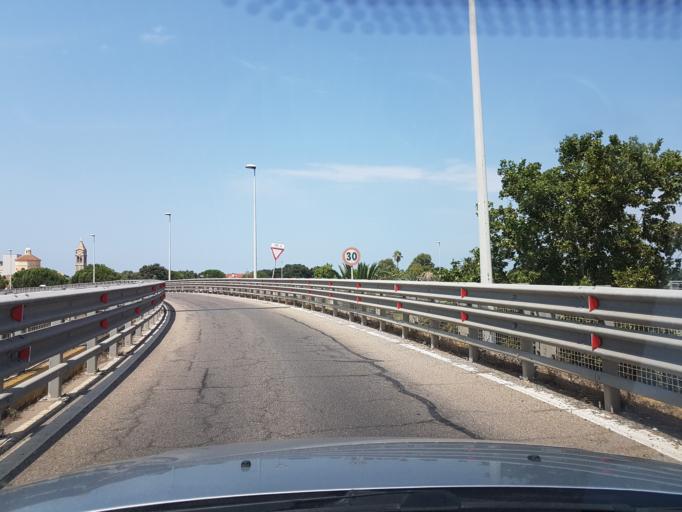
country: IT
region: Sardinia
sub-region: Provincia di Oristano
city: Donigala Fenugheddu
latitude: 39.9268
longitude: 8.5790
